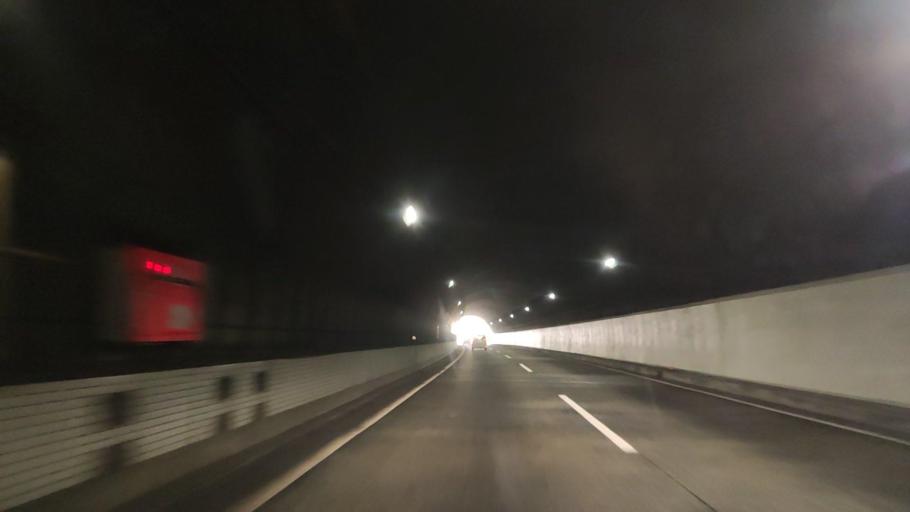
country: JP
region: Okayama
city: Okayama-shi
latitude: 34.6829
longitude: 133.8503
